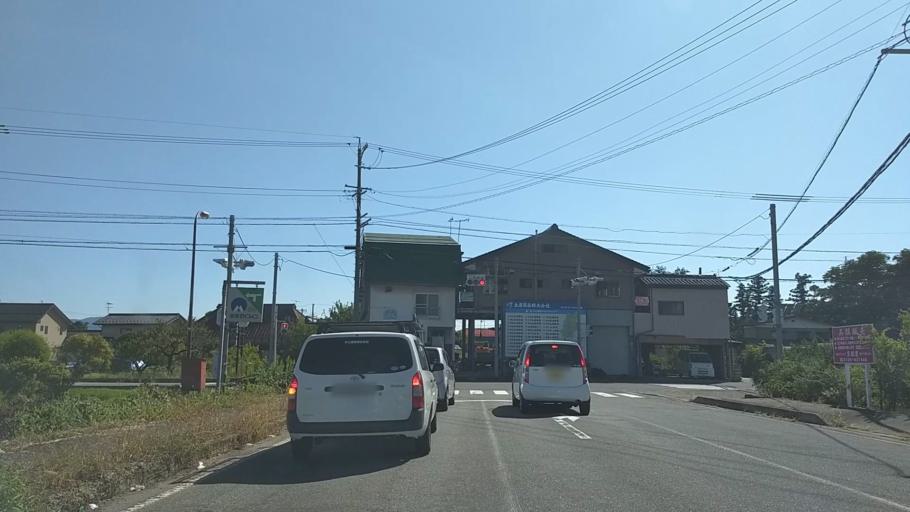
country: JP
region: Nagano
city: Nagano-shi
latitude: 36.6165
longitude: 138.1411
